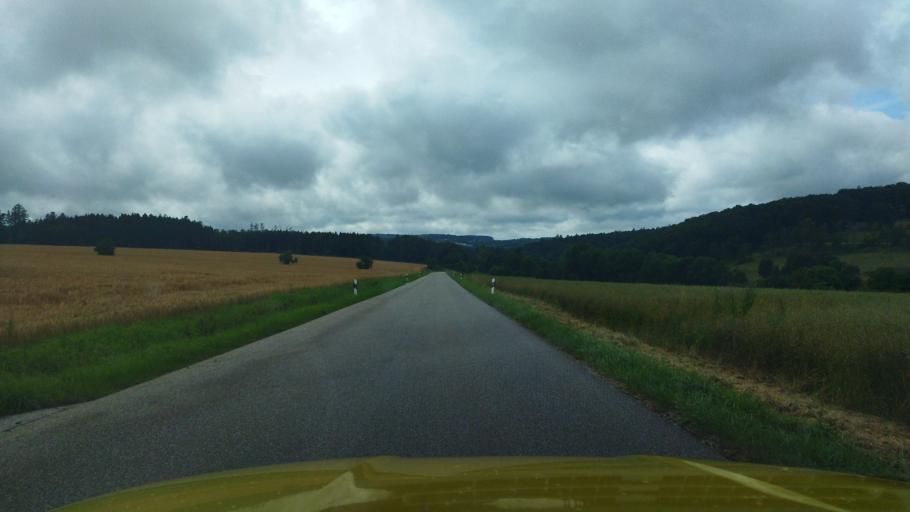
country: DE
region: Bavaria
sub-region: Lower Bavaria
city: Riedenburg
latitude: 48.9430
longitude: 11.7040
